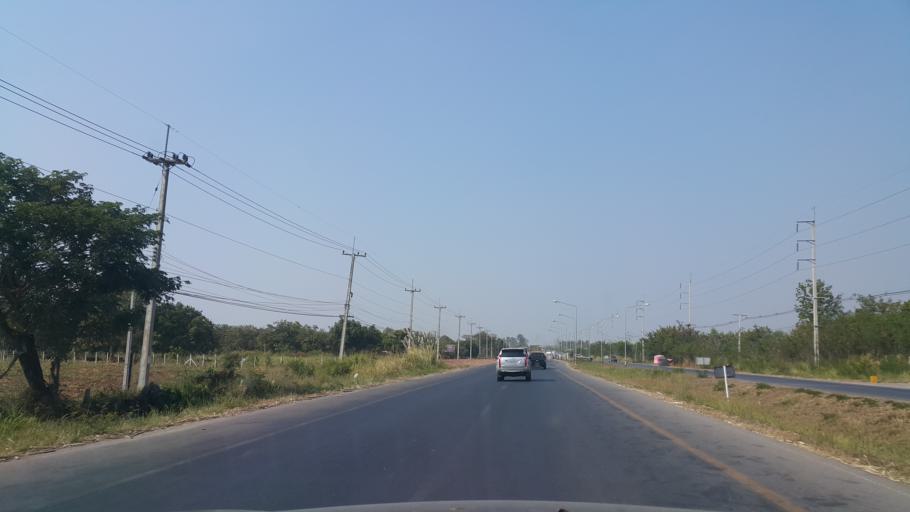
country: TH
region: Chaiyaphum
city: Phu Khiao
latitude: 16.4279
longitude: 102.1292
